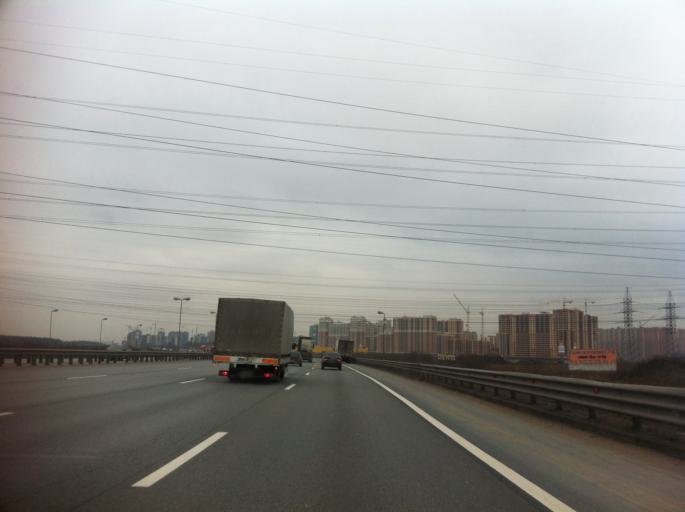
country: RU
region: St.-Petersburg
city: Krasnogvargeisky
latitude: 59.9253
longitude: 30.5301
